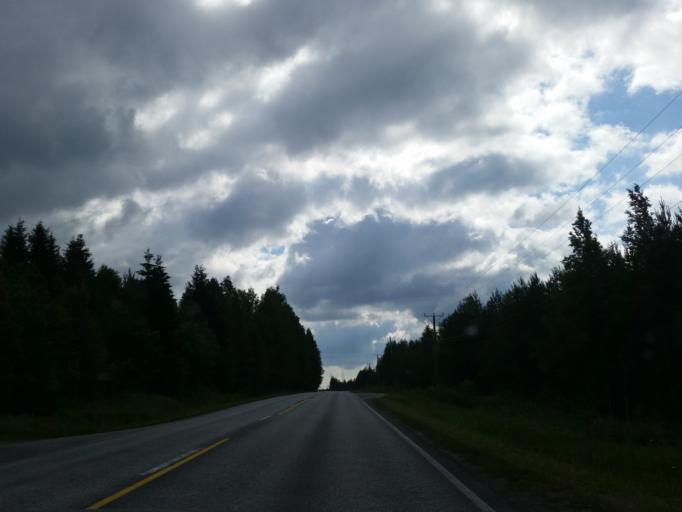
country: FI
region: Northern Savo
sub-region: Kuopio
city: Kuopio
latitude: 62.8444
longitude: 27.4685
